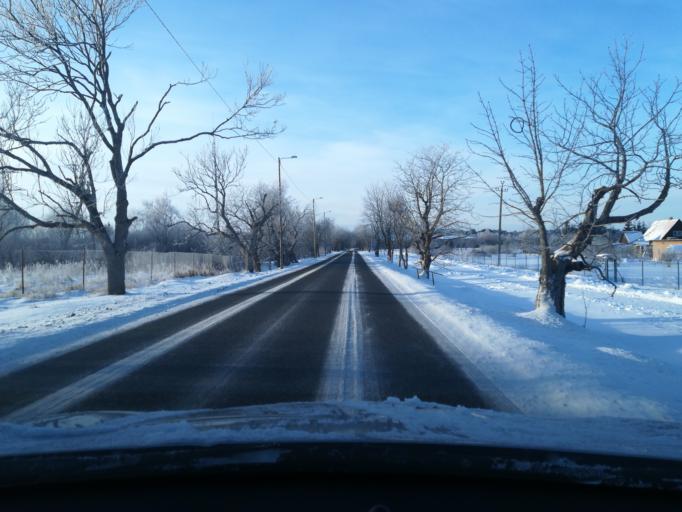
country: EE
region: Harju
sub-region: Keila linn
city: Keila
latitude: 59.3971
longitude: 24.3094
